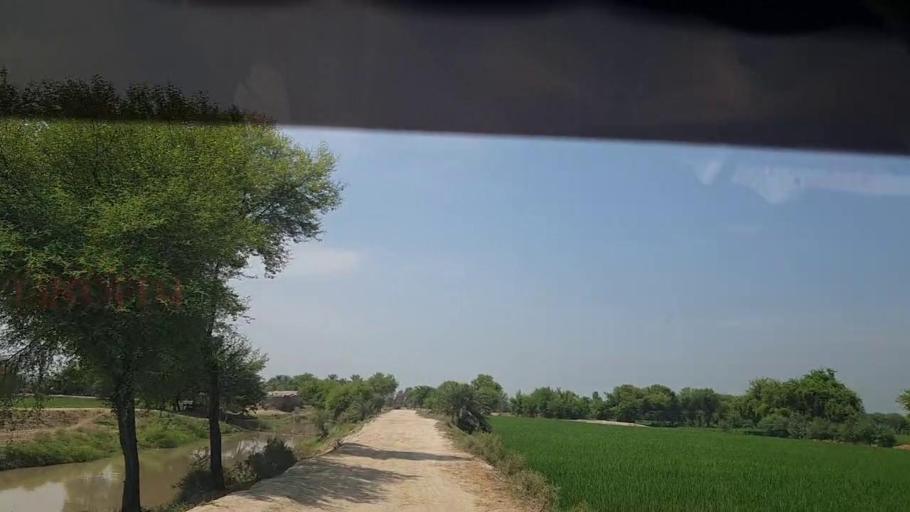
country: PK
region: Sindh
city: Thul
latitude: 28.2021
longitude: 68.6985
